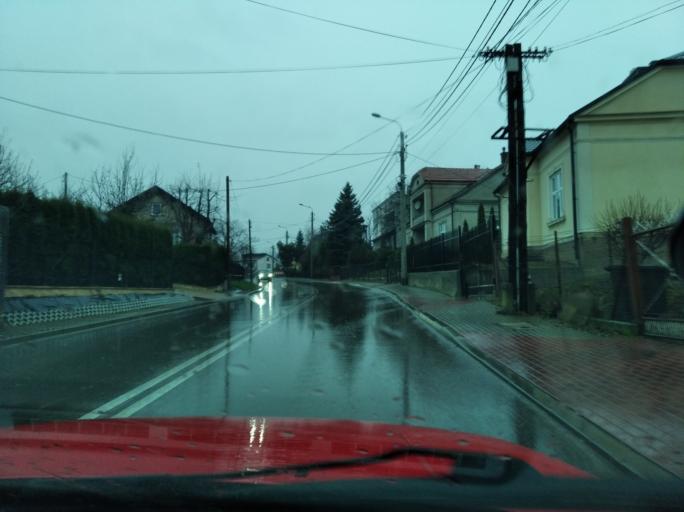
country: PL
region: Subcarpathian Voivodeship
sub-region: Powiat lancucki
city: Lancut
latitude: 50.0700
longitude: 22.2212
